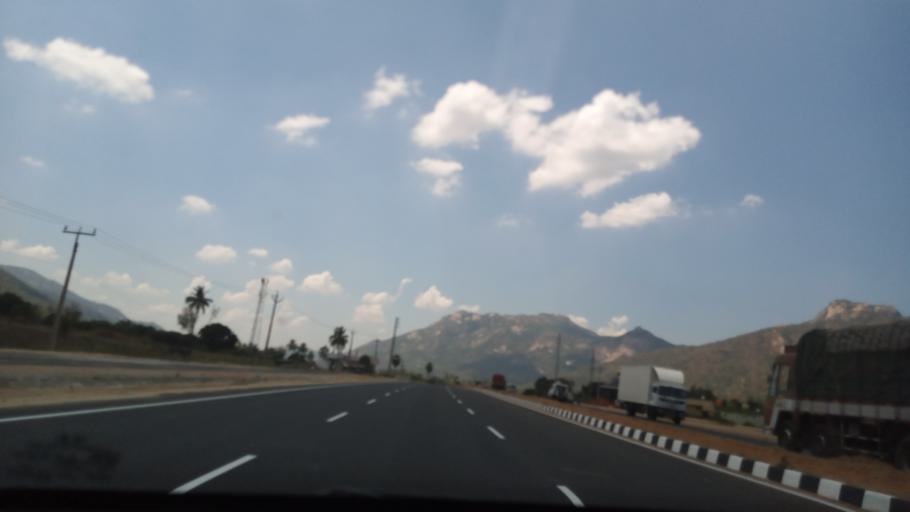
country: IN
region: Andhra Pradesh
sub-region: Chittoor
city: Narasingapuram
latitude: 13.5627
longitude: 79.2557
